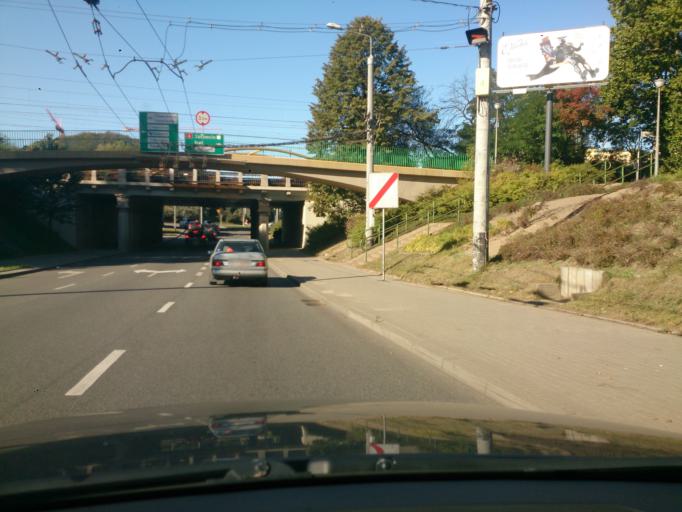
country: PL
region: Pomeranian Voivodeship
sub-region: Gdynia
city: Gdynia
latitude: 54.5096
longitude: 18.5365
